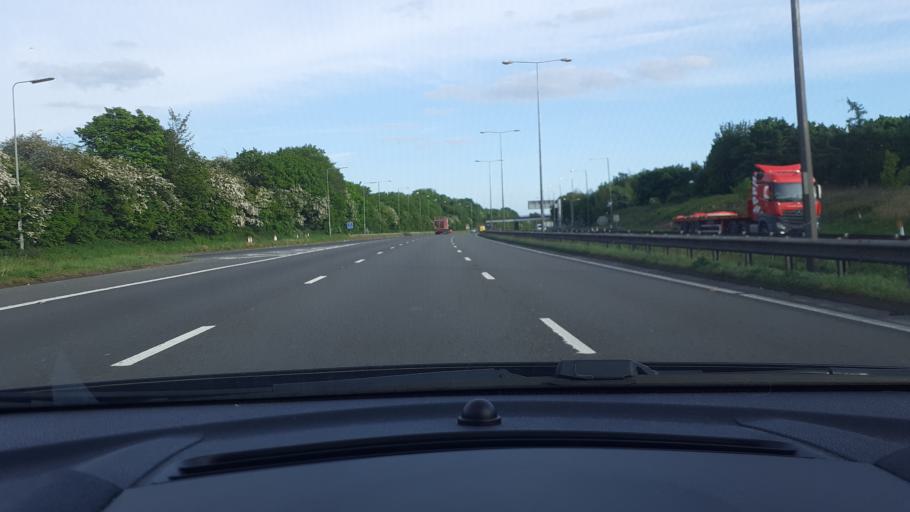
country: GB
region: England
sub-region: Borough of Wigan
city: Ashton in Makerfield
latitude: 53.5050
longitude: -2.6629
